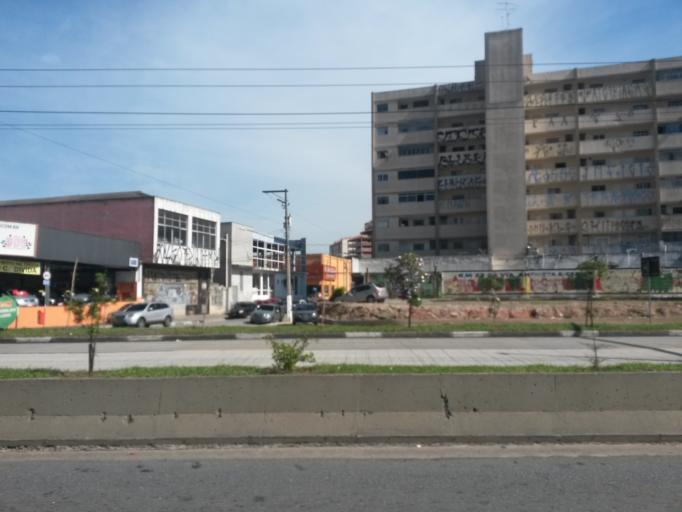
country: BR
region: Sao Paulo
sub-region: Sao Bernardo Do Campo
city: Sao Bernardo do Campo
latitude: -23.7025
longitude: -46.5528
